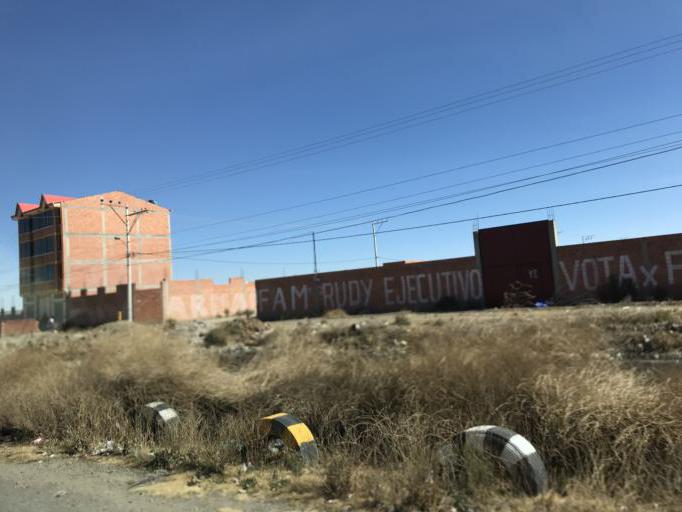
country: BO
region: La Paz
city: La Paz
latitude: -16.5161
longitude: -68.2835
